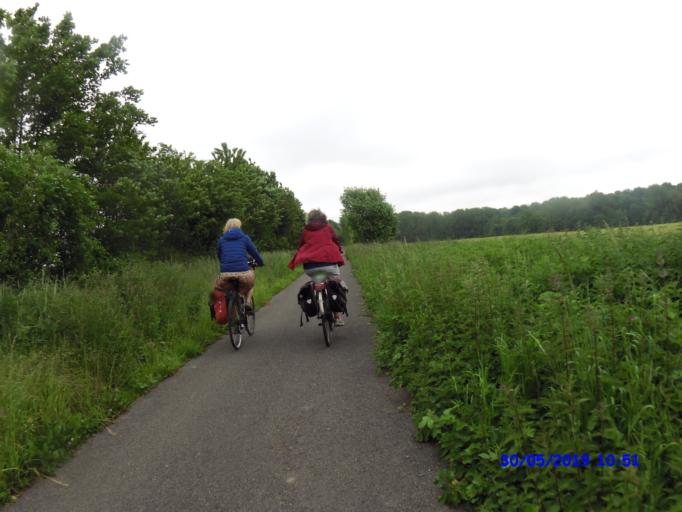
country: BE
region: Wallonia
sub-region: Province du Hainaut
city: Beaumont
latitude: 50.2589
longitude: 4.2808
